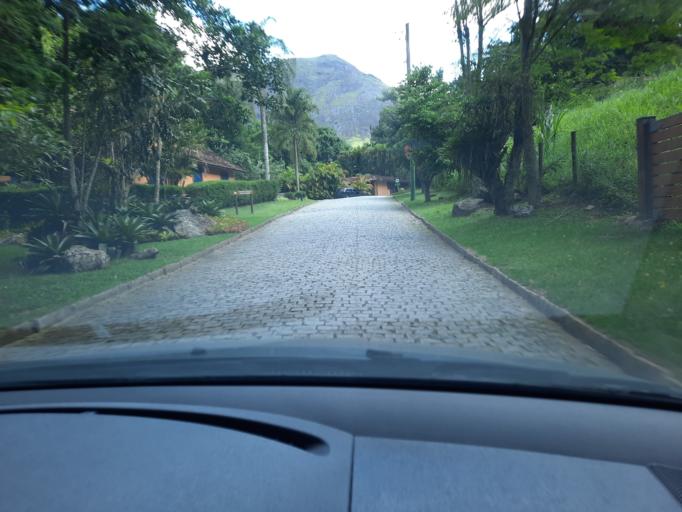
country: BR
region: Rio de Janeiro
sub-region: Petropolis
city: Petropolis
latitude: -22.4376
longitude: -43.1720
